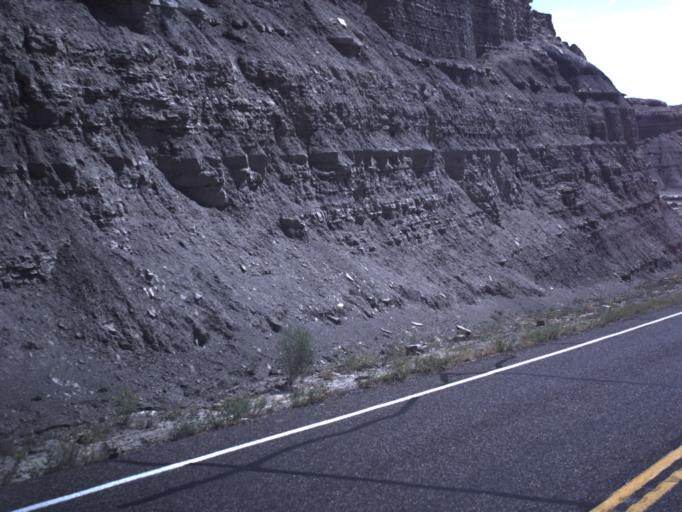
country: US
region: Utah
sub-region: Wayne County
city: Loa
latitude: 38.3650
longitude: -110.8843
